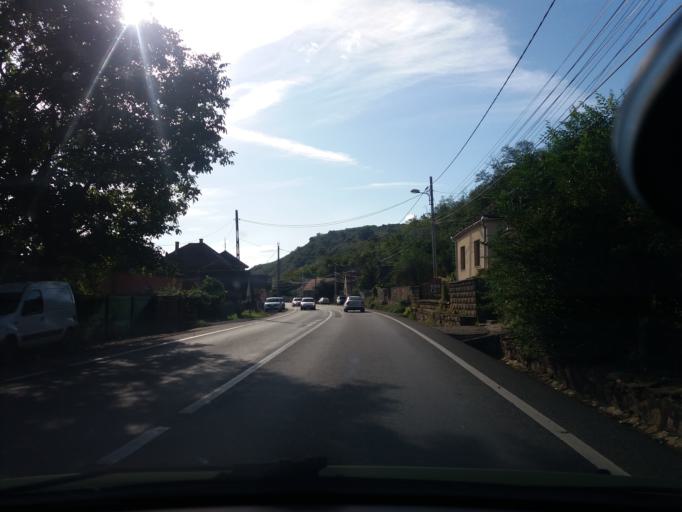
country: RO
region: Arad
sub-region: Oras Lipova
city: Lipova
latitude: 46.1051
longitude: 21.7101
